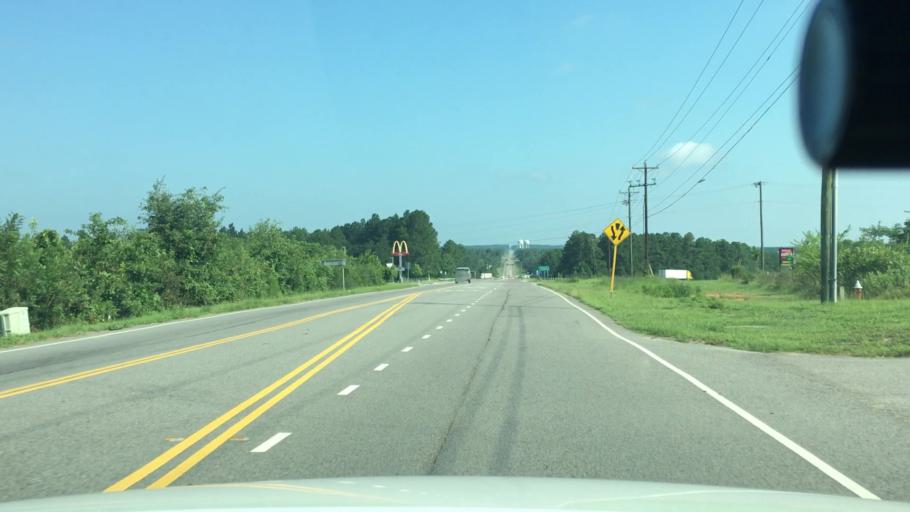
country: US
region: South Carolina
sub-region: Aiken County
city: Graniteville
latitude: 33.6024
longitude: -81.8420
